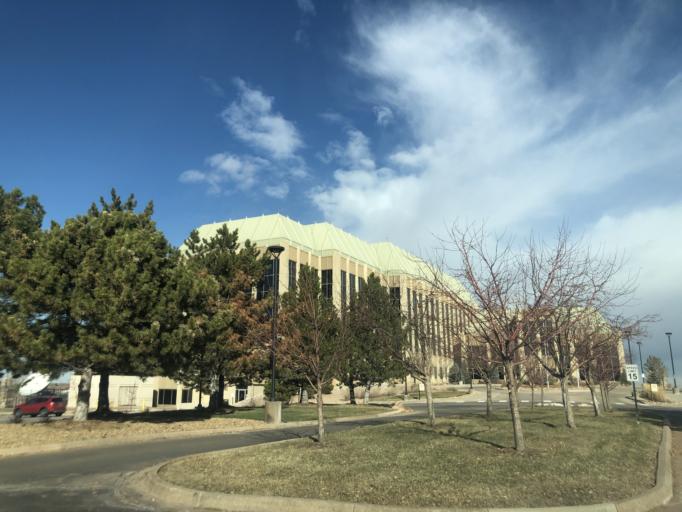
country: US
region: Colorado
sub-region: Douglas County
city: Meridian
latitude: 39.5498
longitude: -104.8563
